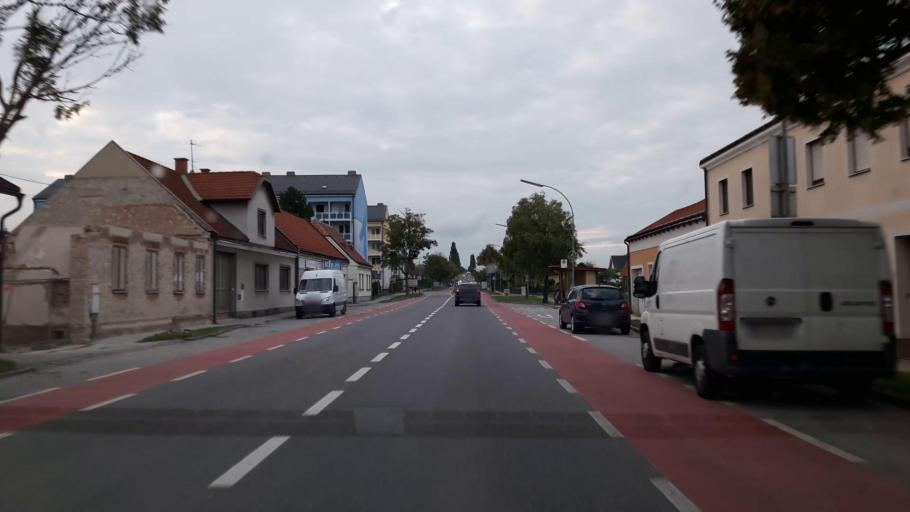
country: AT
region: Lower Austria
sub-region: Politischer Bezirk Wien-Umgebung
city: Schwadorf
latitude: 48.0726
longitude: 16.5806
